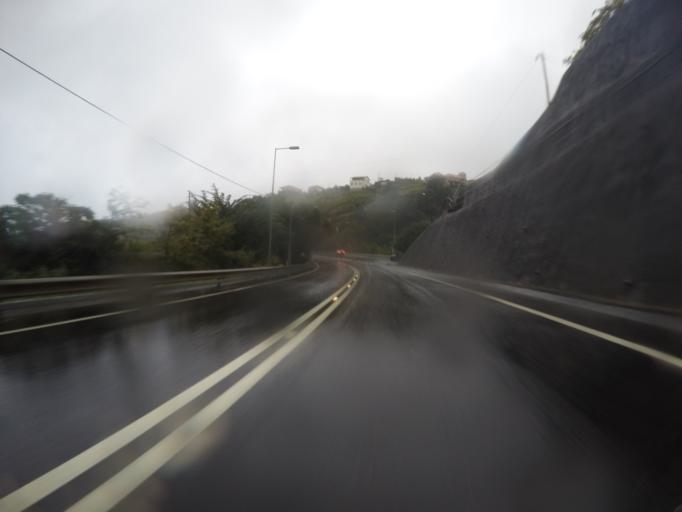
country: PT
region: Madeira
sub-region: Santana
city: Santana
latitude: 32.7638
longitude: -16.8351
